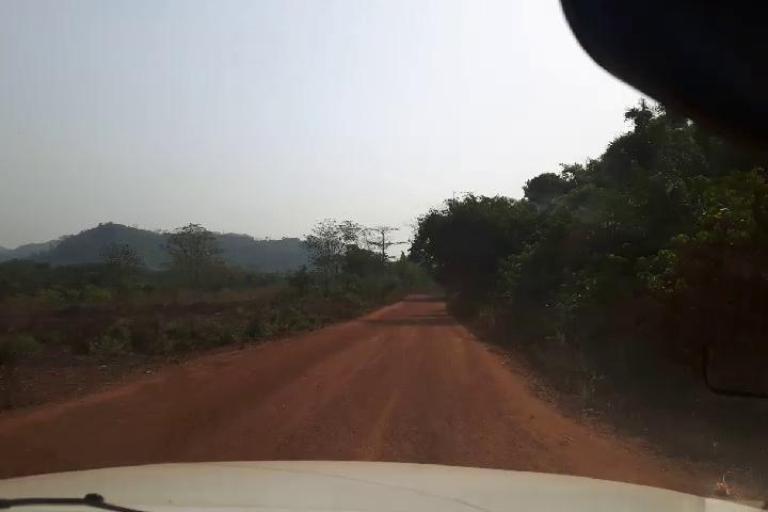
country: SL
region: Northern Province
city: Masingbi
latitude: 8.8587
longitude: -11.8189
